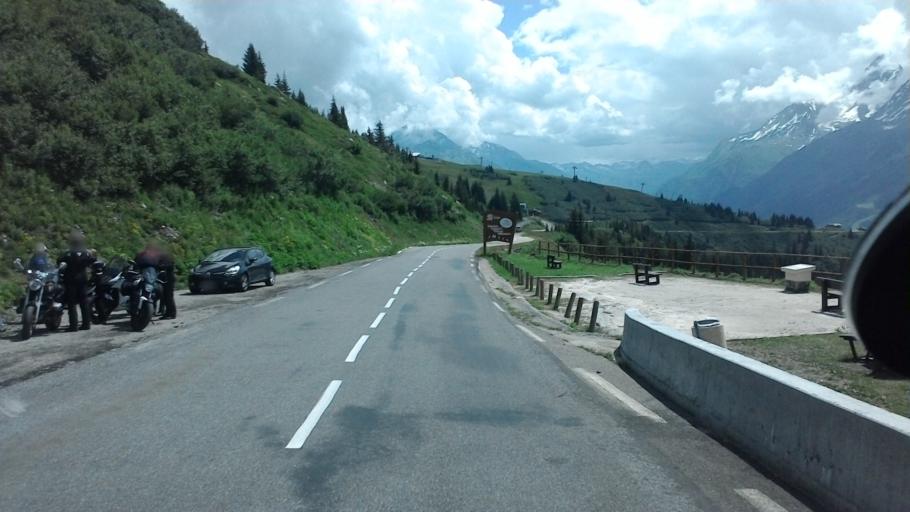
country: FR
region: Rhone-Alpes
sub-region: Departement de la Savoie
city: Seez
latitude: 45.6412
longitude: 6.8446
